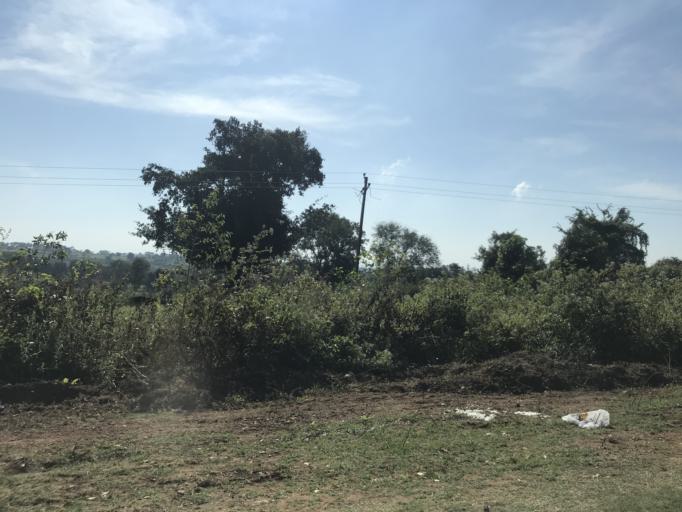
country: IN
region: Karnataka
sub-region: Mysore
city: Heggadadevankote
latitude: 12.0437
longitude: 76.3333
